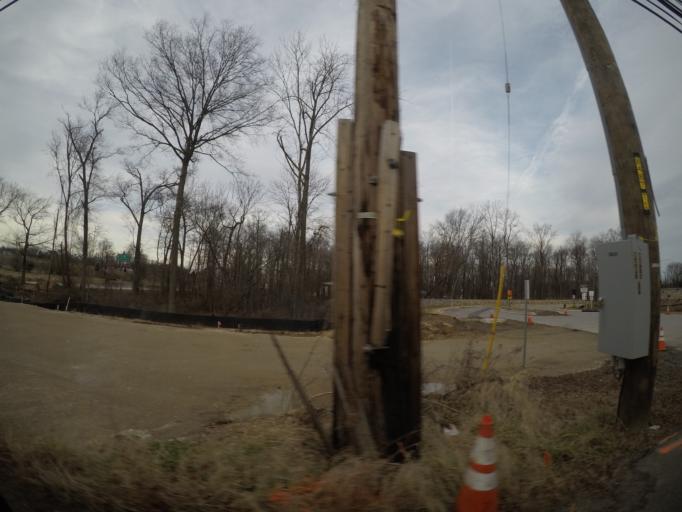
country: US
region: Maryland
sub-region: Anne Arundel County
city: Jessup
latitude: 39.1906
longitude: -76.7711
